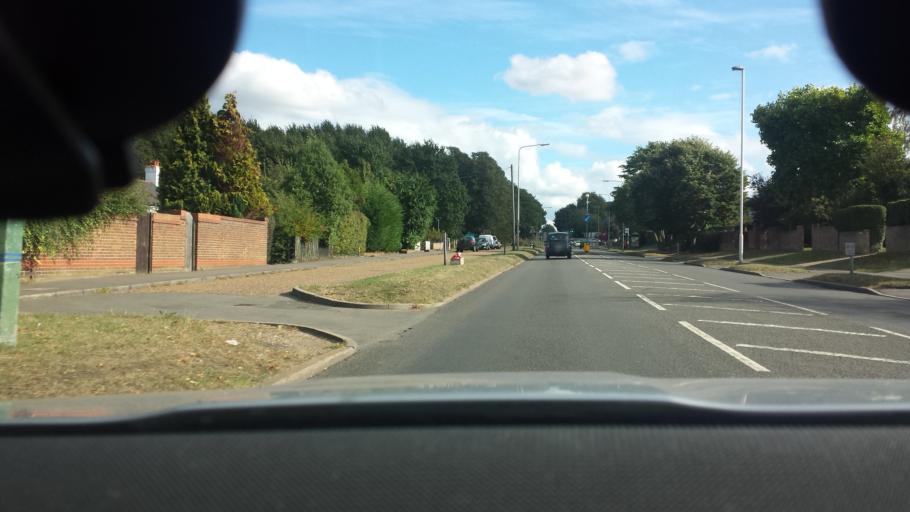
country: GB
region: England
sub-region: Kent
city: Swanley
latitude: 51.4006
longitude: 0.1672
